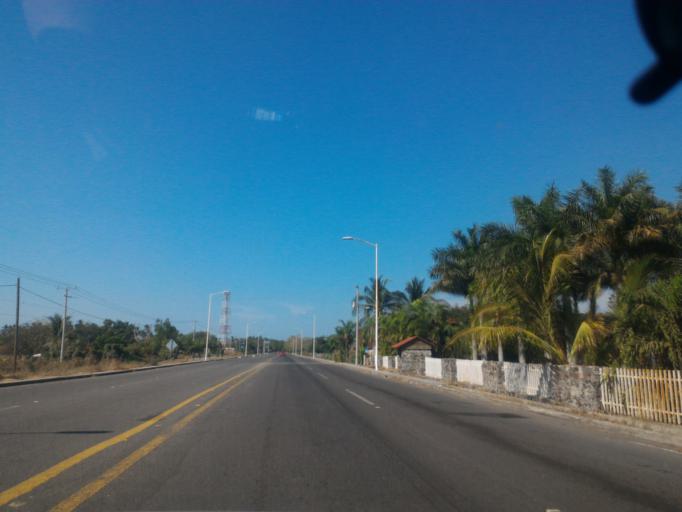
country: MX
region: Colima
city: Tecoman
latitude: 18.9029
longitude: -103.9075
